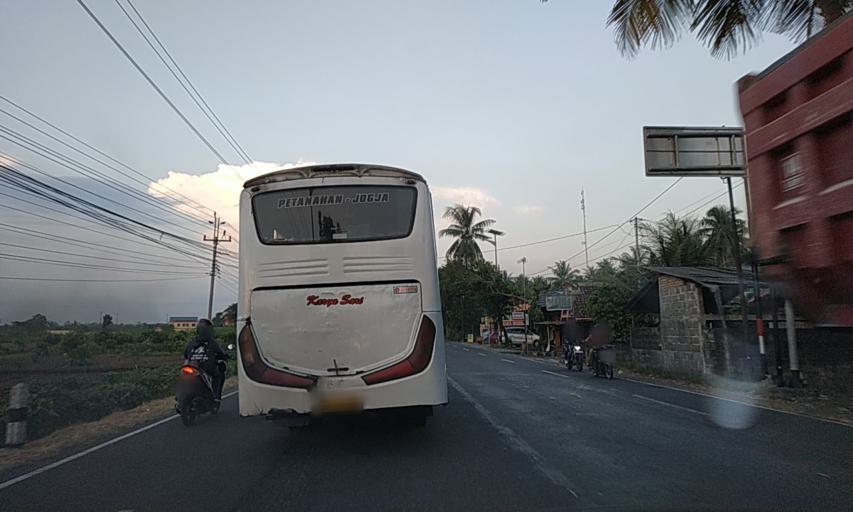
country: ID
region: Daerah Istimewa Yogyakarta
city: Srandakan
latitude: -7.8704
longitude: 110.1432
